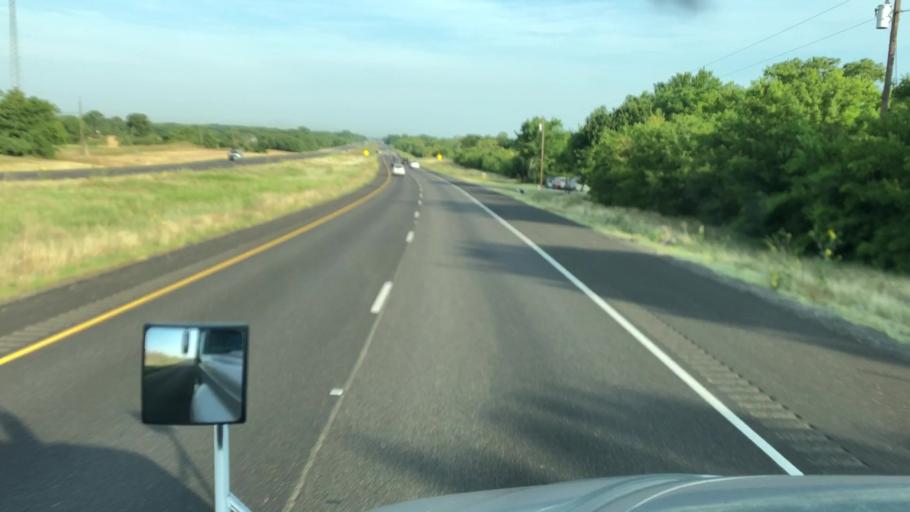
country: US
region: Texas
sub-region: McLennan County
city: Bellmead
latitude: 31.5332
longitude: -97.0224
